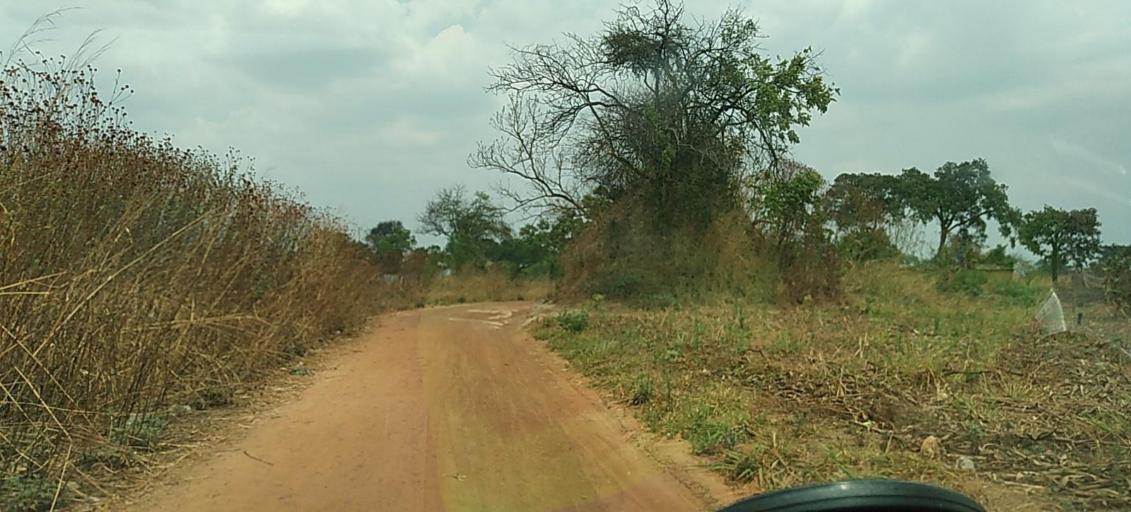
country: ZM
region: North-Western
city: Kansanshi
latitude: -12.0877
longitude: 26.3666
